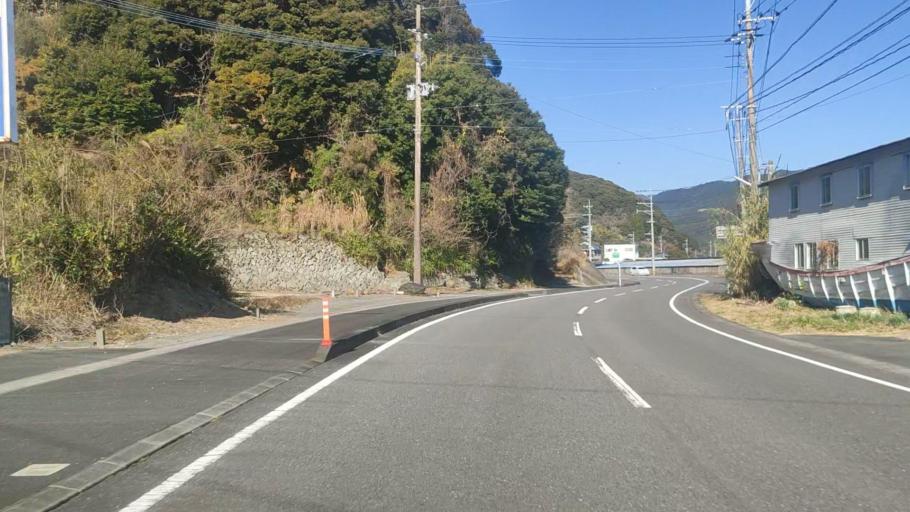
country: JP
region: Oita
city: Saiki
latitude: 32.8266
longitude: 131.9599
